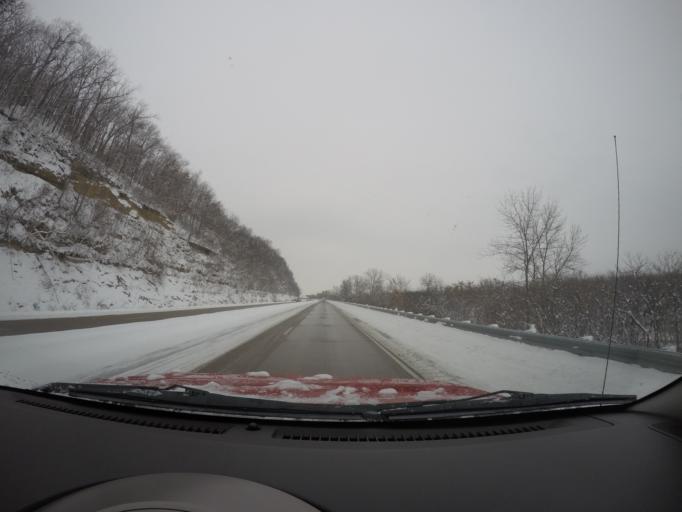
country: US
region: Minnesota
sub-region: Houston County
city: La Crescent
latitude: 43.8399
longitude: -91.2983
